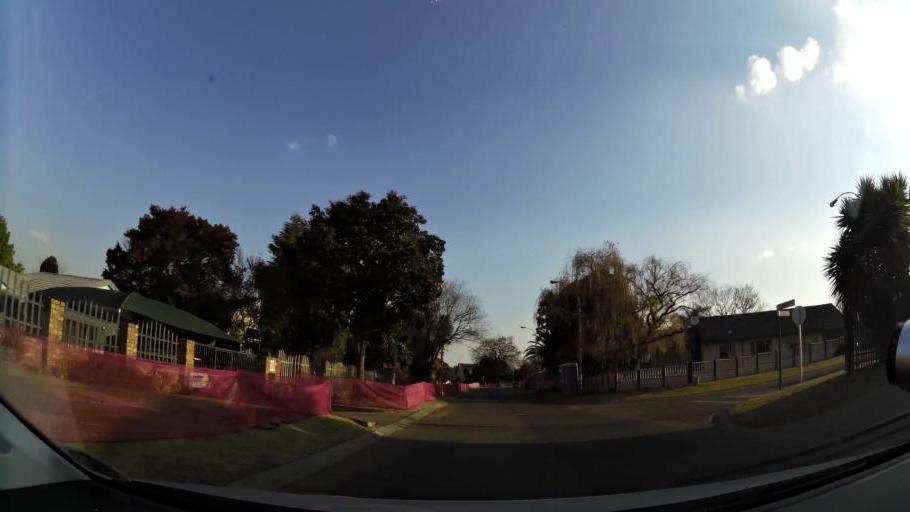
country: ZA
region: Gauteng
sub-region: City of Johannesburg Metropolitan Municipality
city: Modderfontein
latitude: -26.0788
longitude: 28.2208
